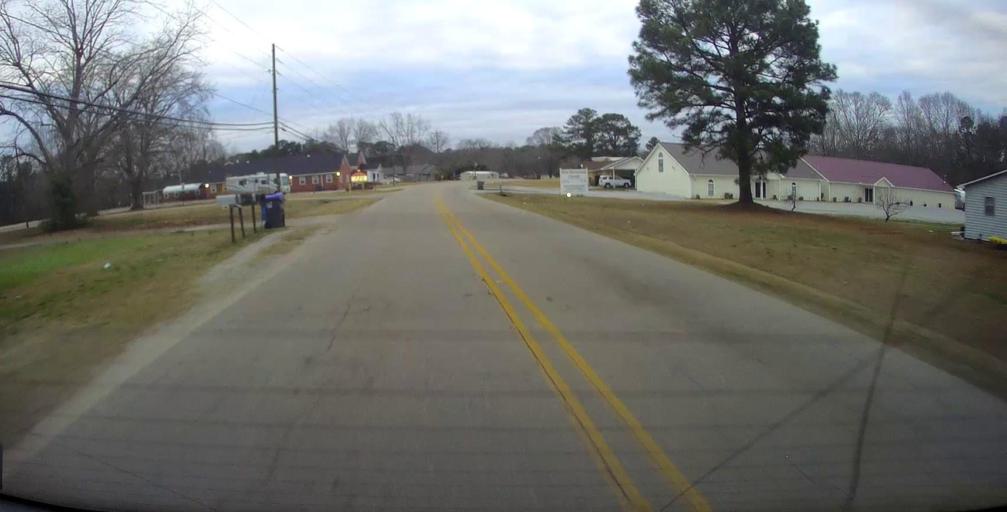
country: US
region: Alabama
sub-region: Chambers County
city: Huguley
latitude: 32.8370
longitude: -85.2317
